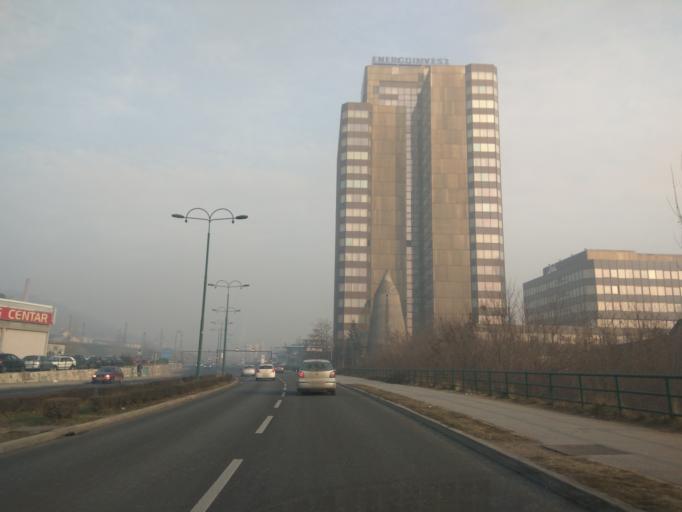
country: BA
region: Federation of Bosnia and Herzegovina
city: Kobilja Glava
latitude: 43.8571
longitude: 18.3891
